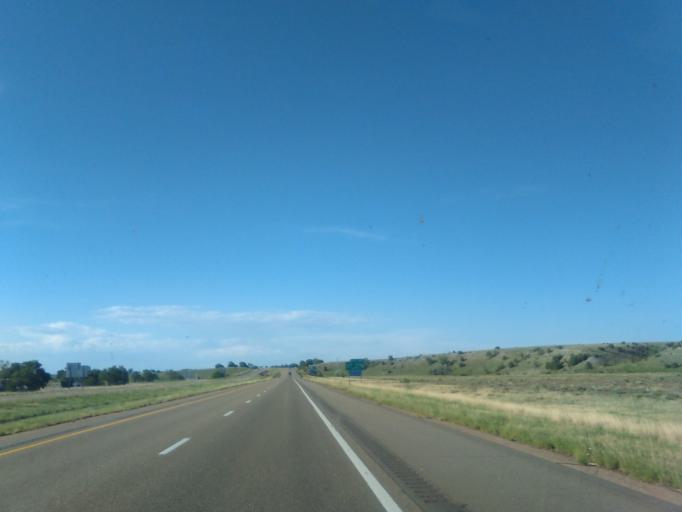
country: US
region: New Mexico
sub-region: San Miguel County
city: Las Vegas
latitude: 35.6059
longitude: -105.2058
